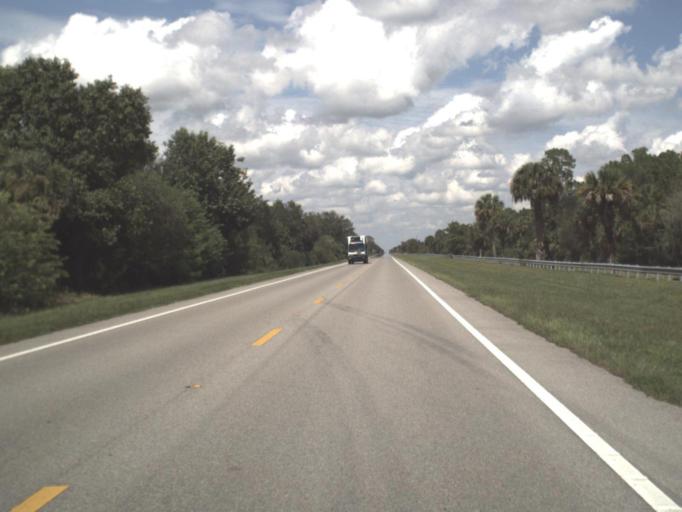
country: US
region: Florida
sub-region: Collier County
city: Immokalee
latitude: 26.2775
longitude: -81.3423
